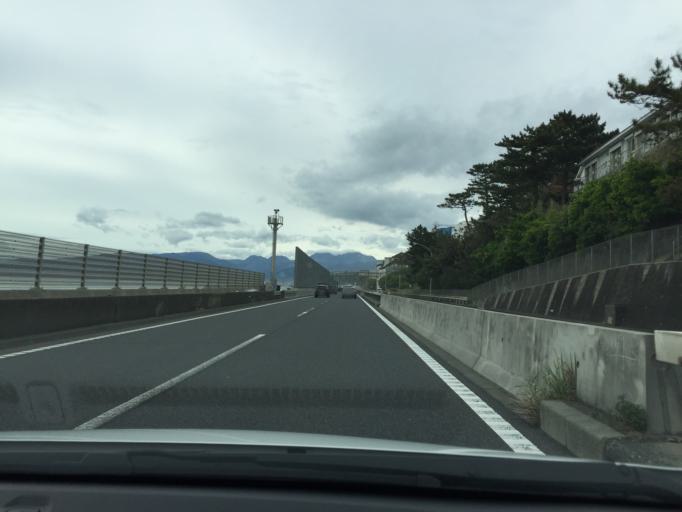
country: JP
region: Kanagawa
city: Ninomiya
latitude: 35.2950
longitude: 139.2565
